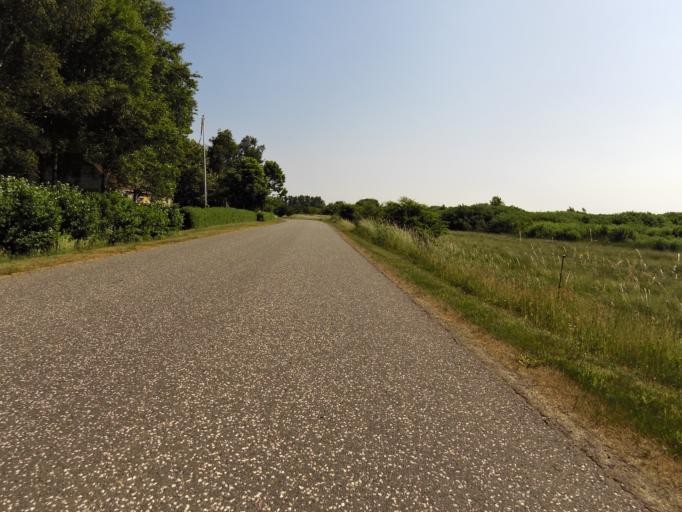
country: DK
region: Central Jutland
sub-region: Holstebro Kommune
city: Vinderup
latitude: 56.5698
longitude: 8.7813
